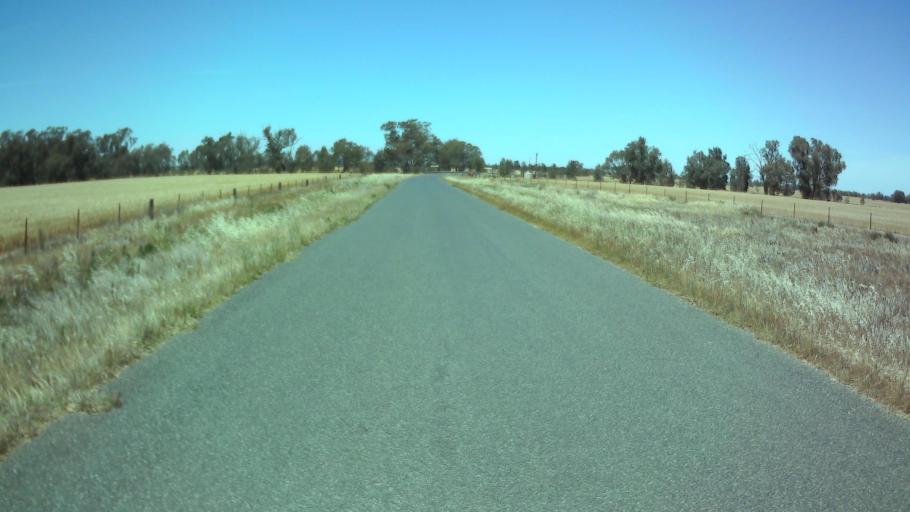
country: AU
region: New South Wales
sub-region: Weddin
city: Grenfell
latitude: -34.0368
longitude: 147.7898
